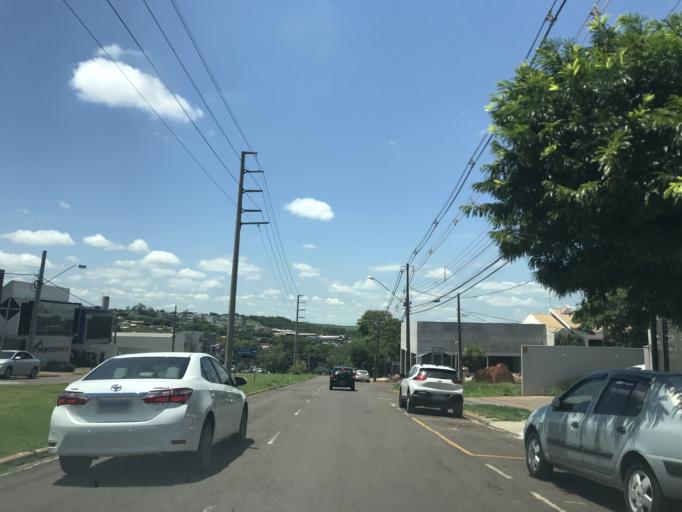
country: BR
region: Parana
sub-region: Maringa
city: Maringa
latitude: -23.4509
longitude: -51.9324
